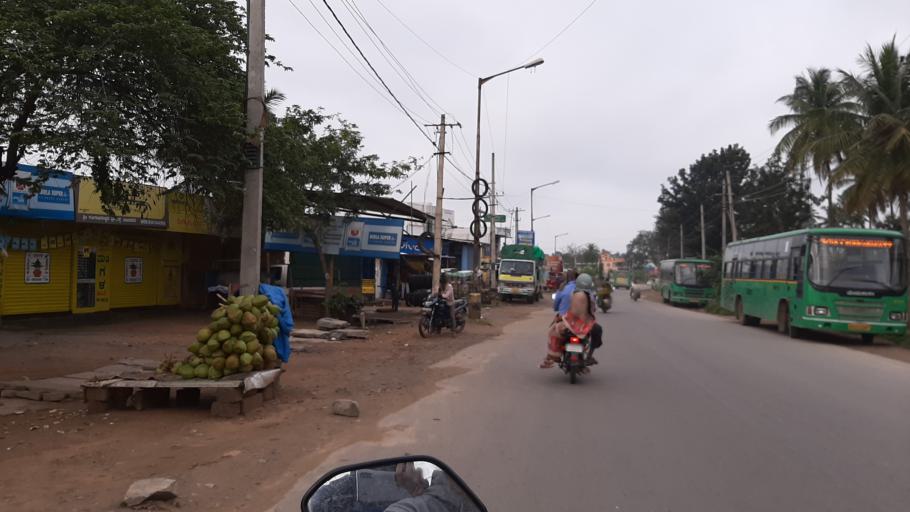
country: IN
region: Karnataka
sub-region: Bangalore Rural
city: Nelamangala
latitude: 12.9654
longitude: 77.3988
